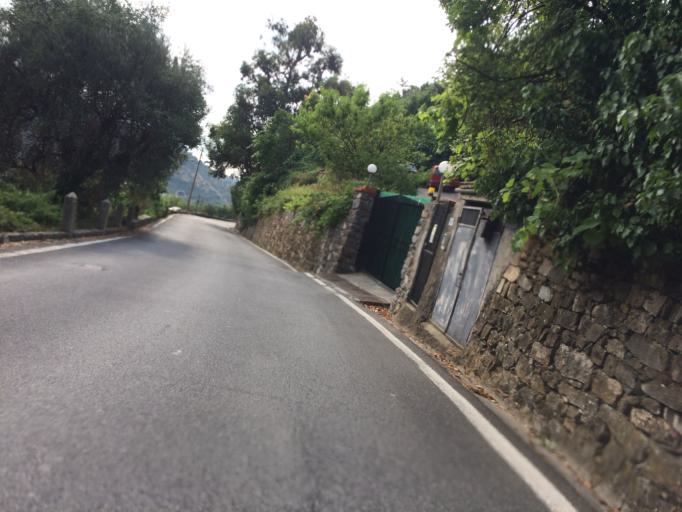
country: IT
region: Liguria
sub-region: Provincia di Imperia
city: San Remo
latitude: 43.8376
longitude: 7.7554
